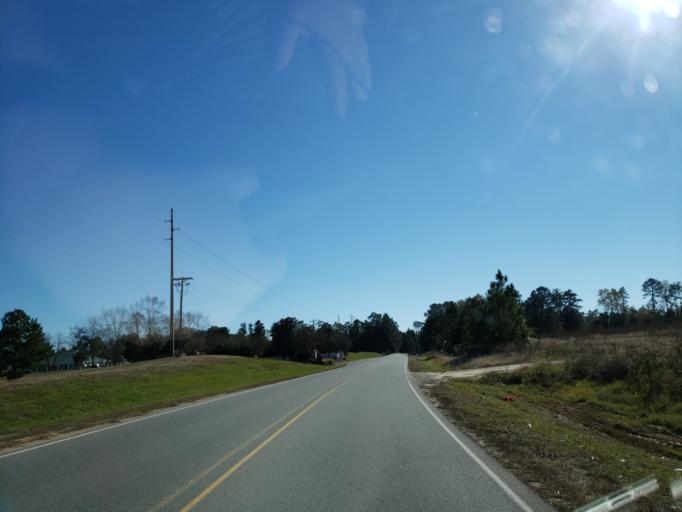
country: US
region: Mississippi
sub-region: Lamar County
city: West Hattiesburg
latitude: 31.3238
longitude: -89.3992
